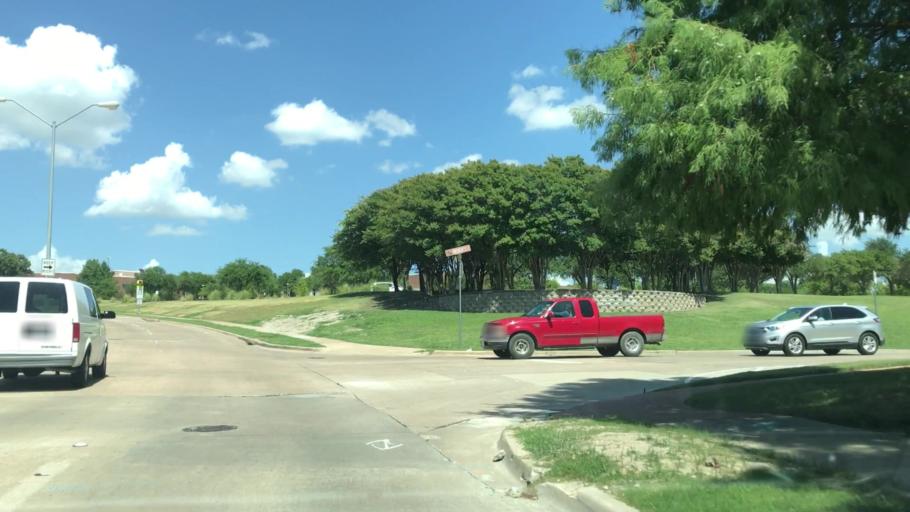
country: US
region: Texas
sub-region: Rockwall County
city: Rockwall
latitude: 32.9043
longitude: -96.4618
